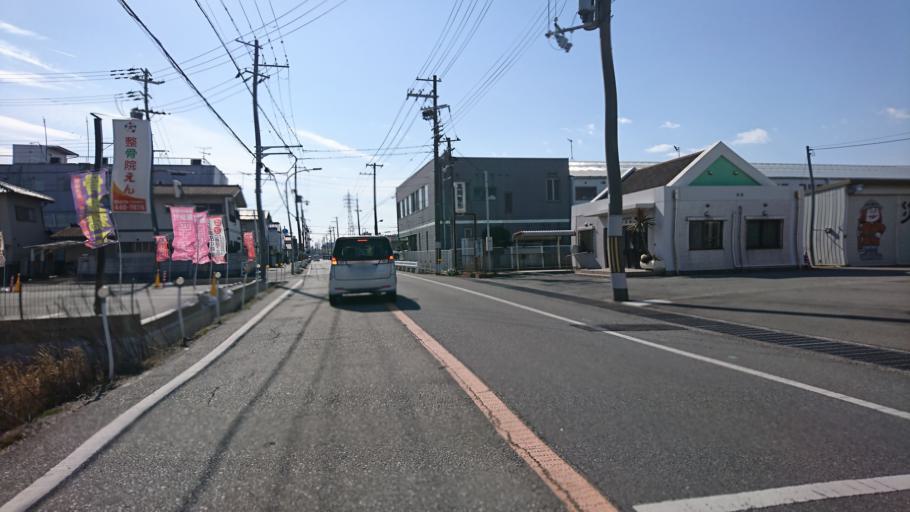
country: JP
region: Hyogo
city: Kakogawacho-honmachi
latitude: 34.7923
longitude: 134.8253
